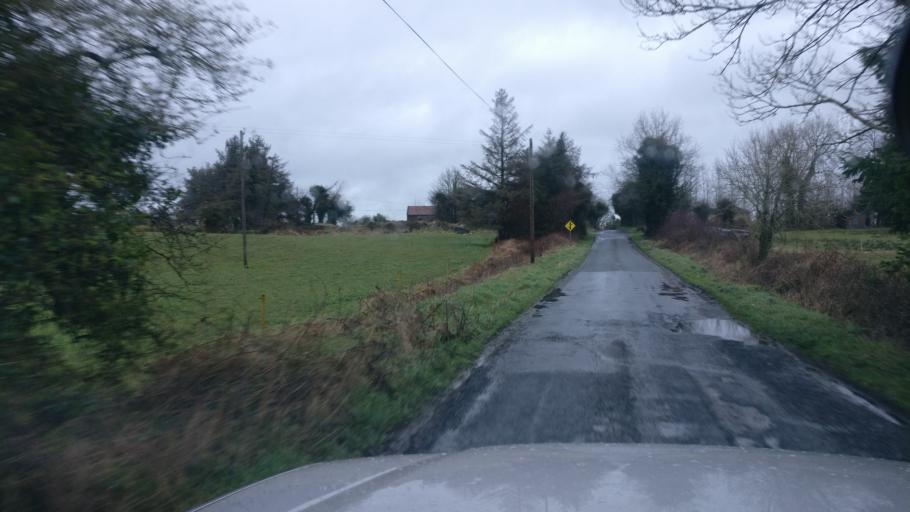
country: IE
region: Connaught
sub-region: County Galway
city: Ballinasloe
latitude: 53.2509
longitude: -8.3556
